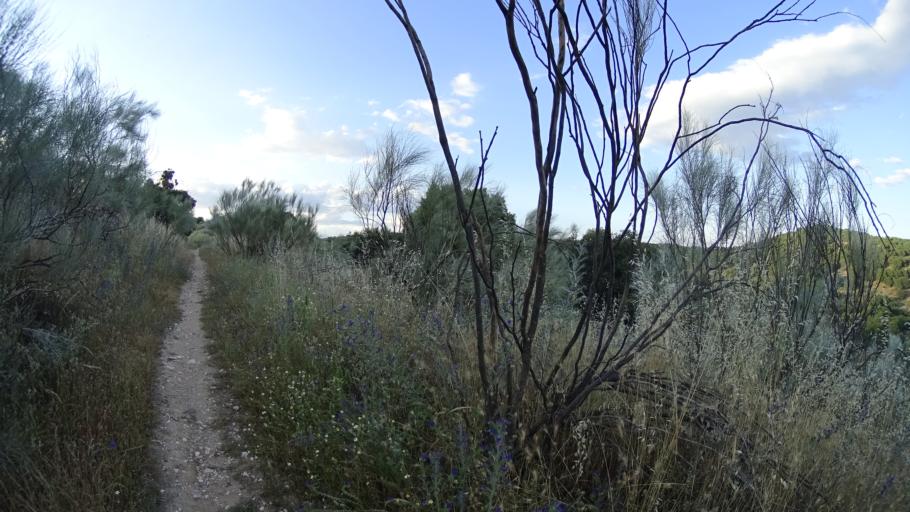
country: ES
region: Madrid
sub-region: Provincia de Madrid
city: Colmenarejo
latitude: 40.5273
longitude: -3.9933
